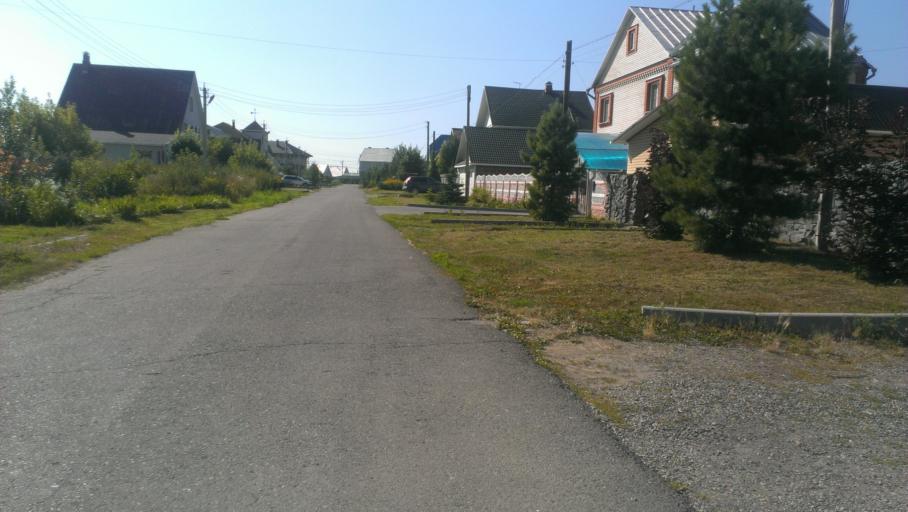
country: RU
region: Altai Krai
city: Novosilikatnyy
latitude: 53.3703
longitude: 83.6552
